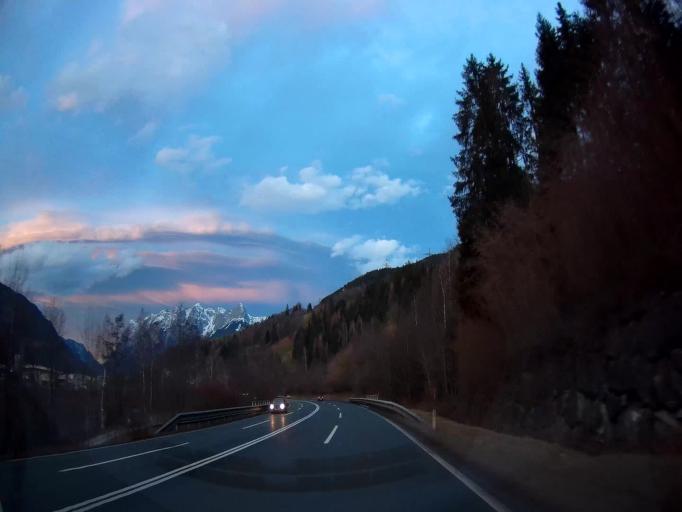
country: AT
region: Salzburg
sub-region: Politischer Bezirk Sankt Johann im Pongau
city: Bischofshofen
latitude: 47.3958
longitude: 13.2263
